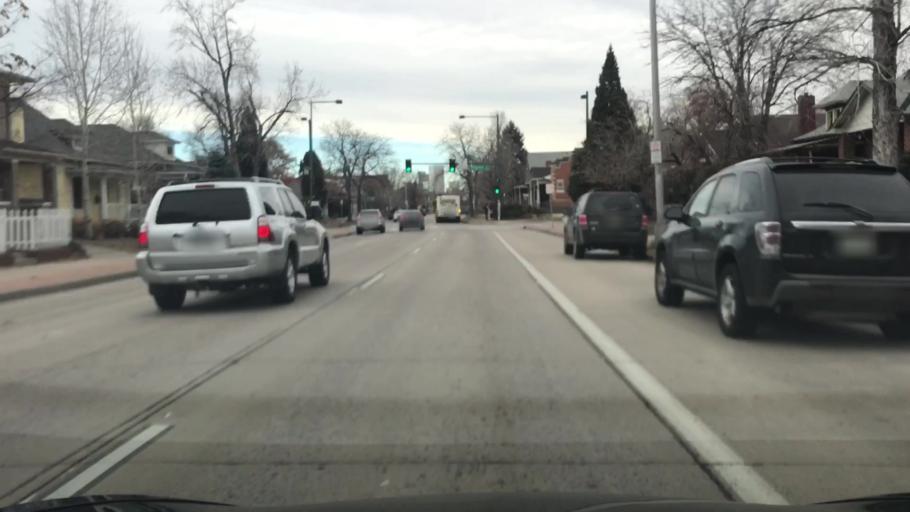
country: US
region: Colorado
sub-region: Denver County
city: Denver
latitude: 39.7068
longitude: -104.9863
